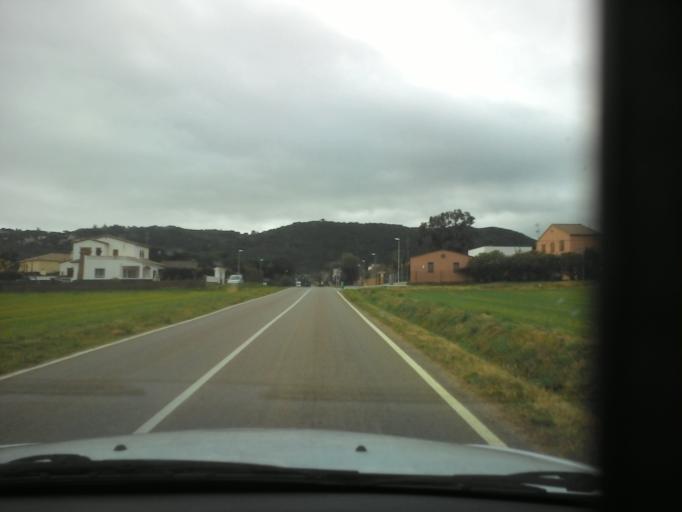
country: ES
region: Catalonia
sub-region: Provincia de Girona
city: Calonge
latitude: 41.8559
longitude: 3.0625
